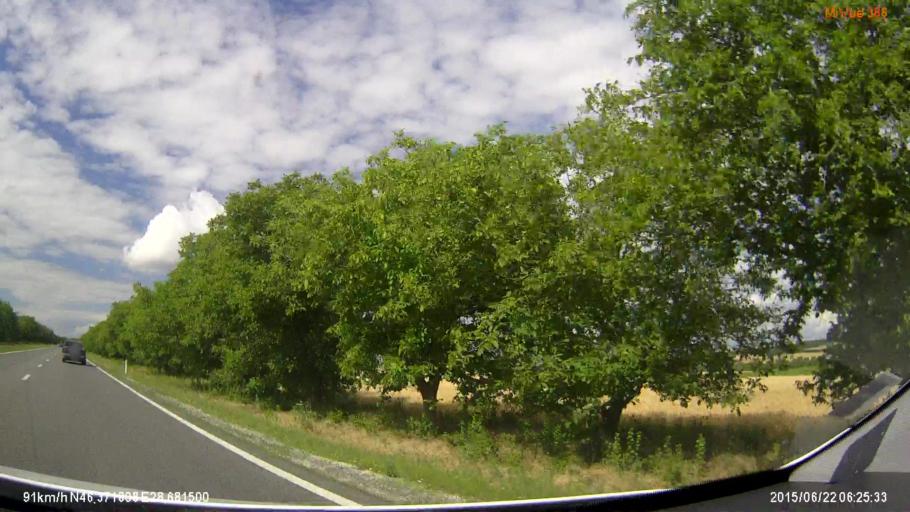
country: MD
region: Gagauzia
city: Bugeac
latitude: 46.3714
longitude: 28.6815
